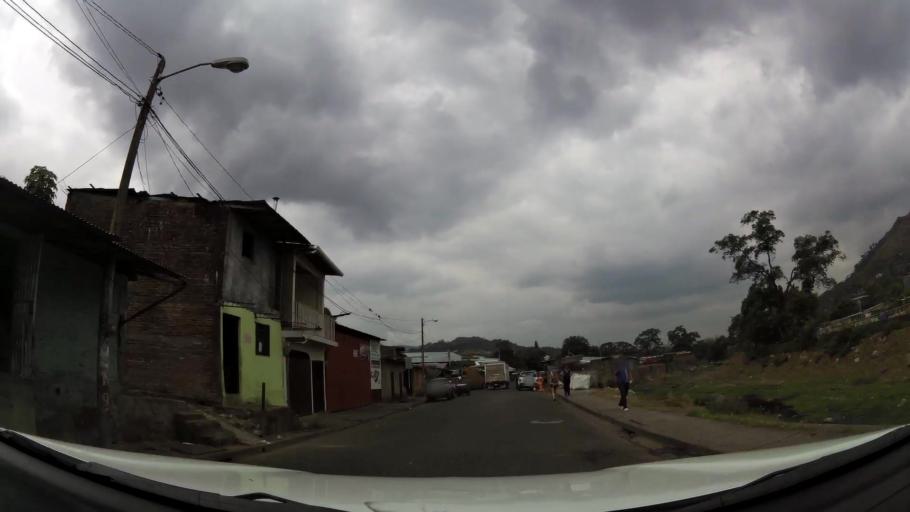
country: NI
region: Matagalpa
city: Matagalpa
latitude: 12.9222
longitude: -85.9243
